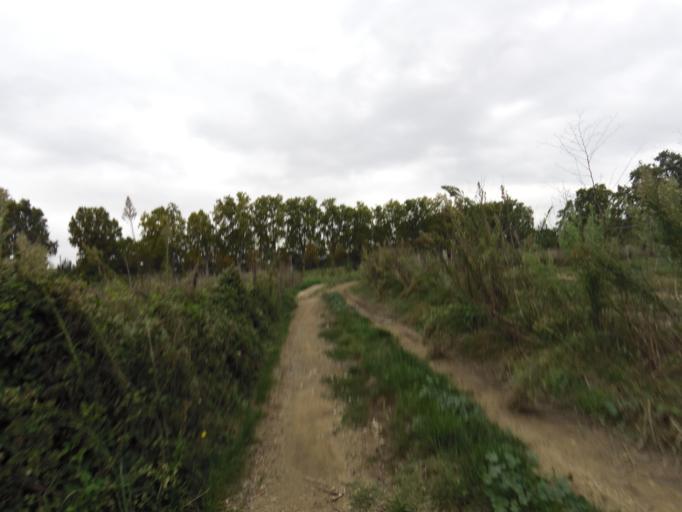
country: FR
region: Languedoc-Roussillon
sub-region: Departement de l'Herault
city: Villetelle
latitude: 43.7348
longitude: 4.1423
